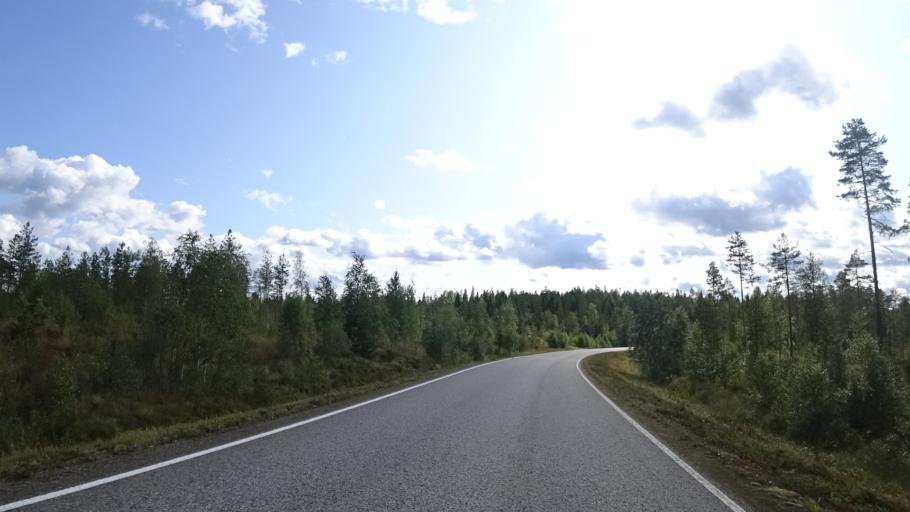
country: RU
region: Republic of Karelia
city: Vyartsilya
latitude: 62.2635
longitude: 30.7753
